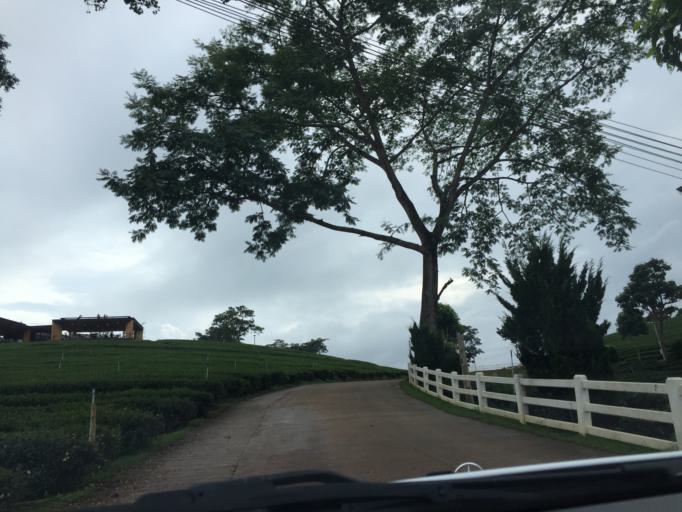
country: TH
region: Chiang Rai
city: Mae Chan
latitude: 20.2002
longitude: 99.8183
